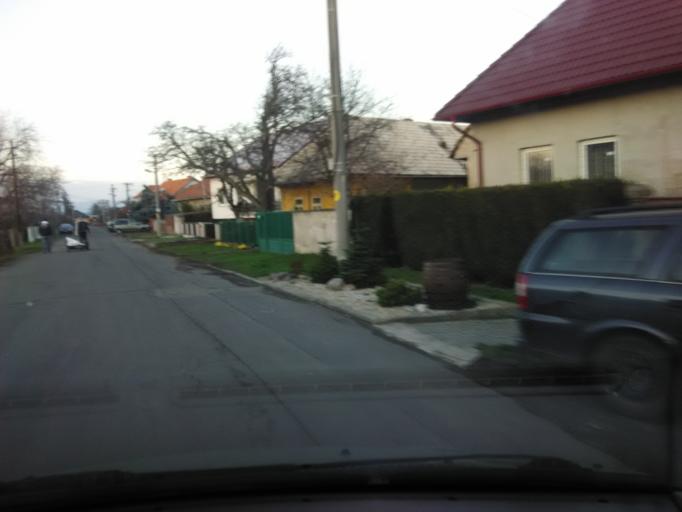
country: SK
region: Nitriansky
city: Tlmace
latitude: 48.2710
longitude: 18.5418
